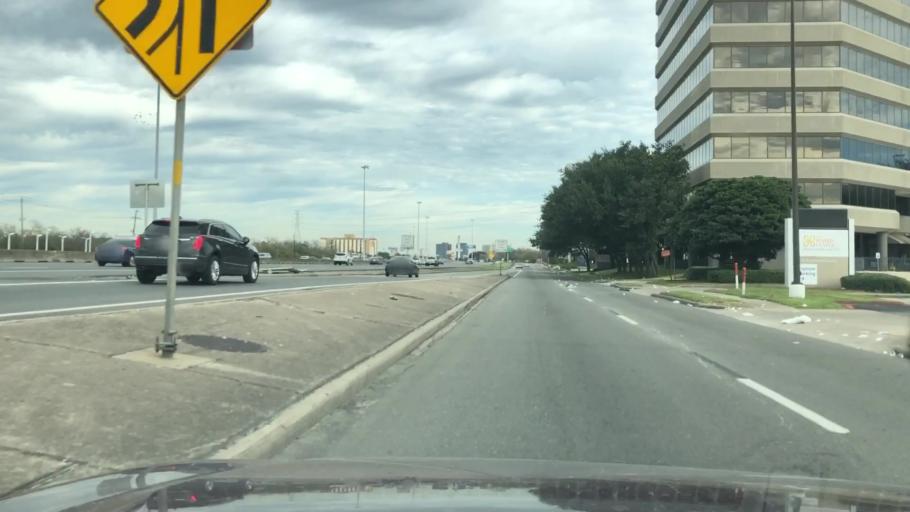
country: US
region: Texas
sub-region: Fort Bend County
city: Meadows Place
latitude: 29.6780
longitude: -95.5392
